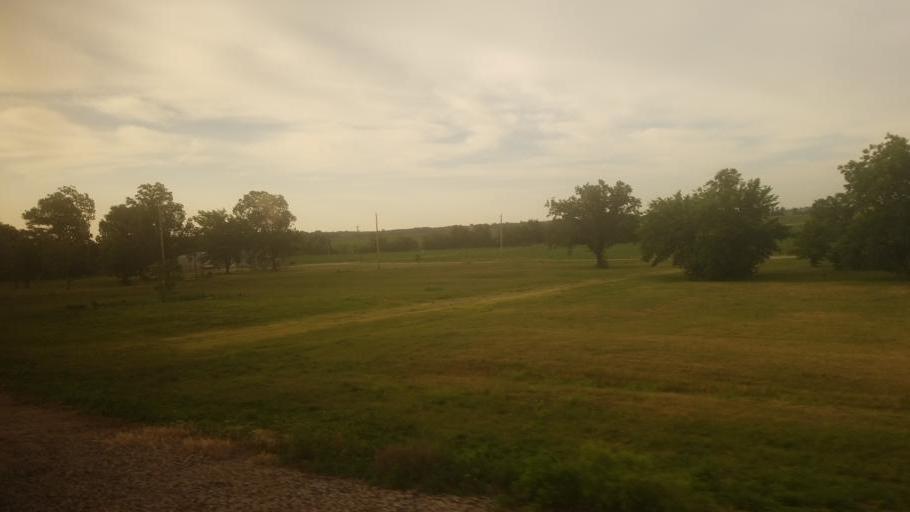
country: US
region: Kansas
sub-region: Osage County
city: Osage City
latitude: 38.5179
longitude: -95.9573
